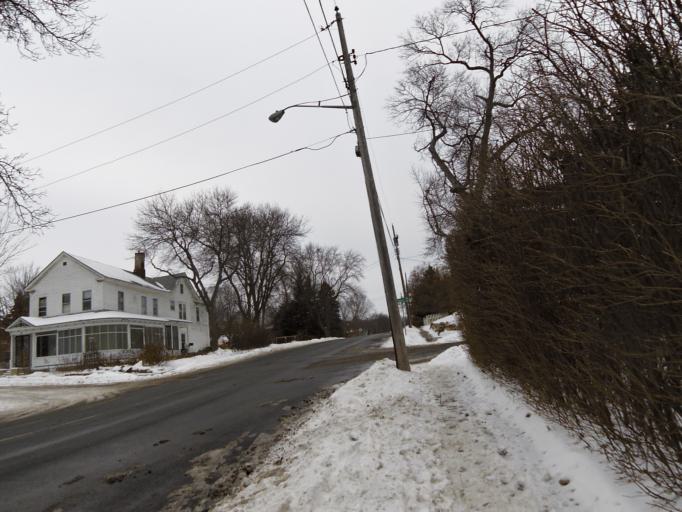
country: US
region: Minnesota
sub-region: Washington County
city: Stillwater
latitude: 45.0594
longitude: -92.8117
